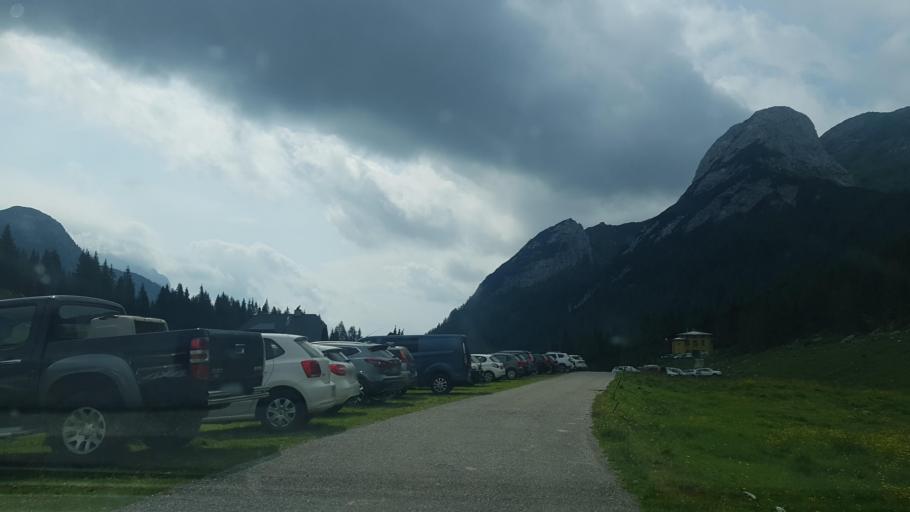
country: IT
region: Friuli Venezia Giulia
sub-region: Provincia di Udine
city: Paularo
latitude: 46.5670
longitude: 13.1703
